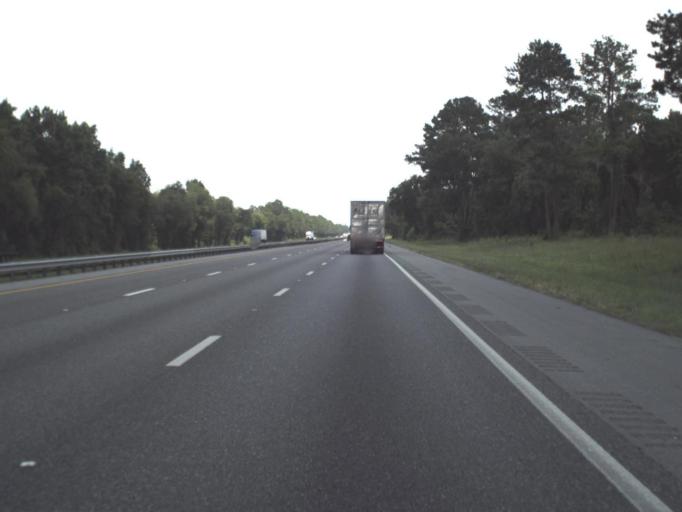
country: US
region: Florida
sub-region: Hamilton County
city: Jasper
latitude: 30.4677
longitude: -82.9645
